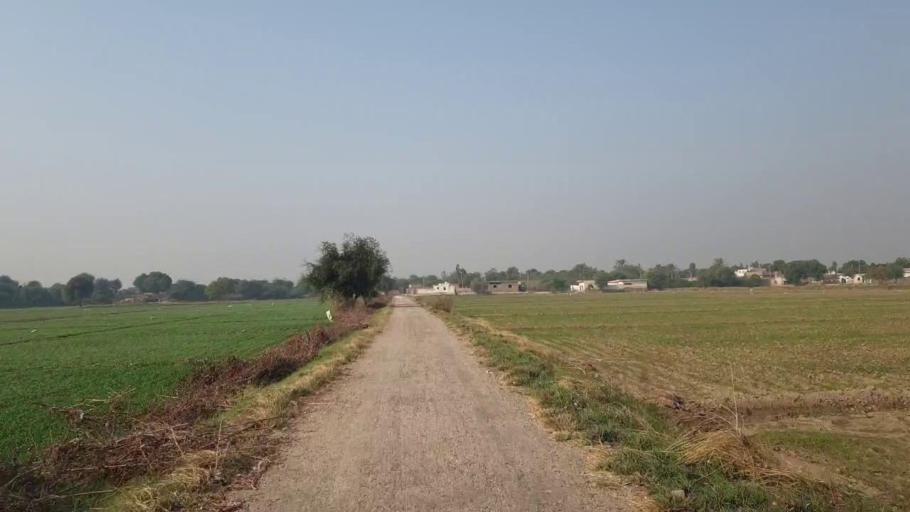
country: PK
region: Sindh
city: Kotri
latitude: 25.3317
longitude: 68.3267
